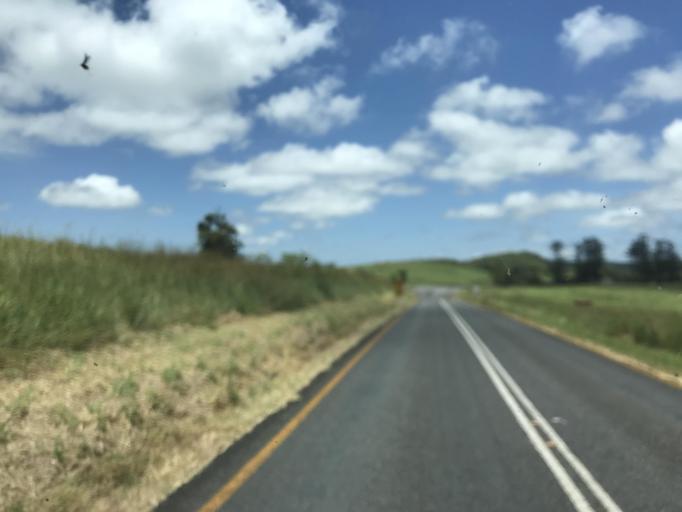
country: AU
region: Queensland
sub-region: Tablelands
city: Ravenshoe
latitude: -17.5244
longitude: 145.5441
